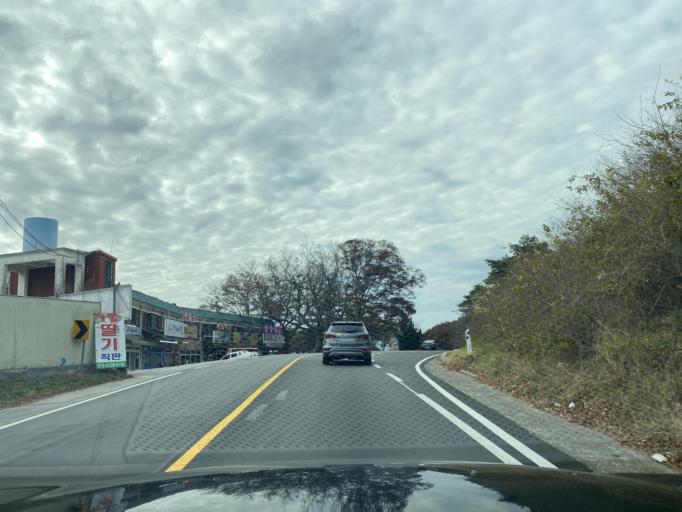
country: KR
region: Chungcheongnam-do
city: Hongsung
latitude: 36.6617
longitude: 126.6313
